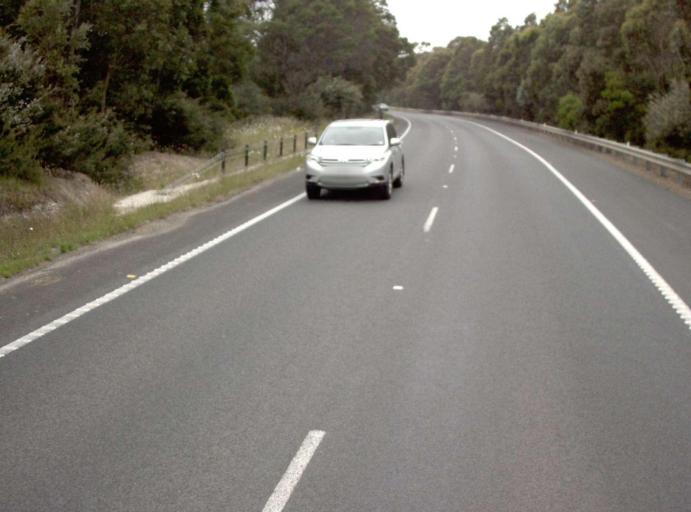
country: AU
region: Victoria
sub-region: Latrobe
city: Moe
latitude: -38.2060
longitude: 146.3032
